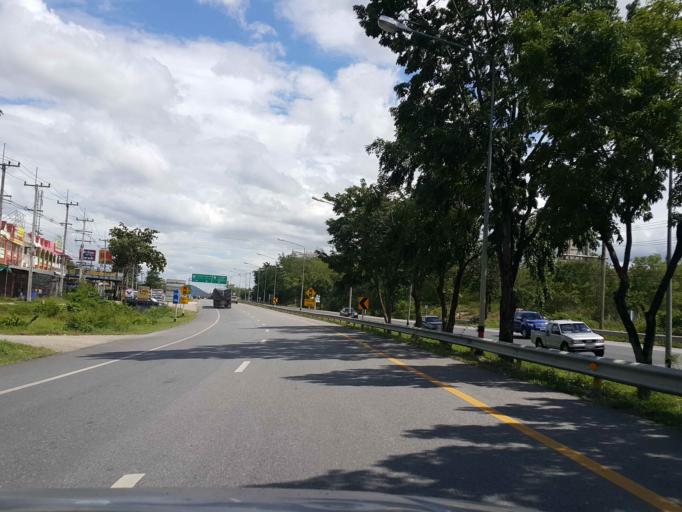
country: TH
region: Tak
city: Tak
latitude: 16.8455
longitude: 99.1119
